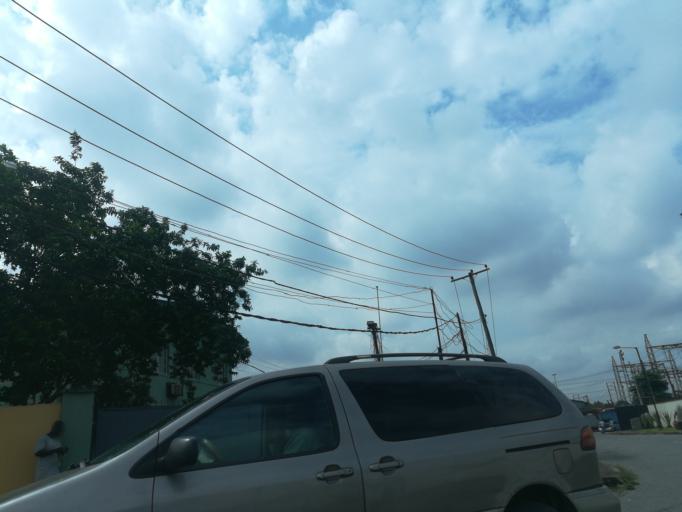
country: NG
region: Lagos
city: Oshodi
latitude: 6.5602
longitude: 3.3620
